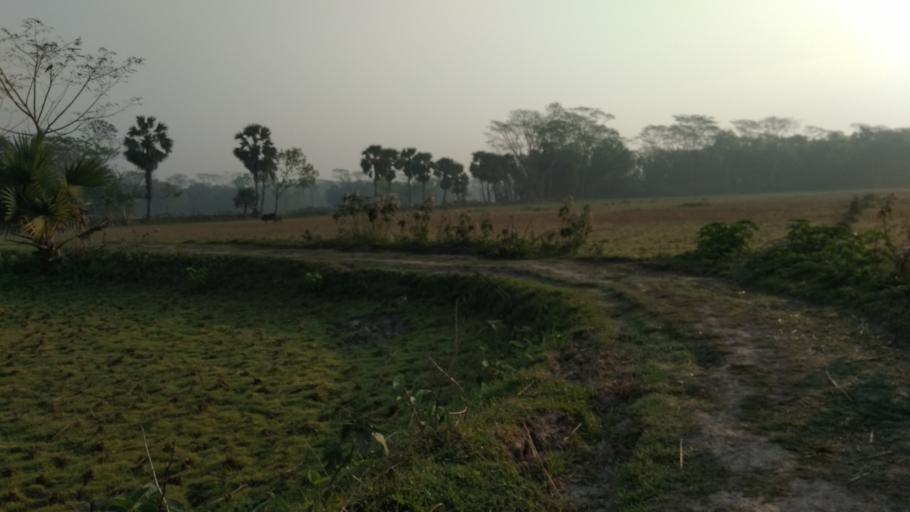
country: BD
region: Barisal
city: Mehendiganj
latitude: 22.9359
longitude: 90.4138
